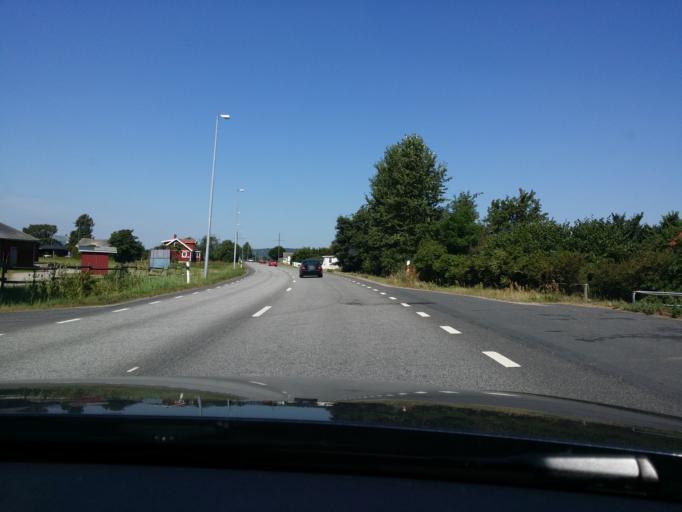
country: SE
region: Blekinge
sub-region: Solvesborgs Kommun
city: Soelvesborg
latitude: 56.0479
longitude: 14.6591
